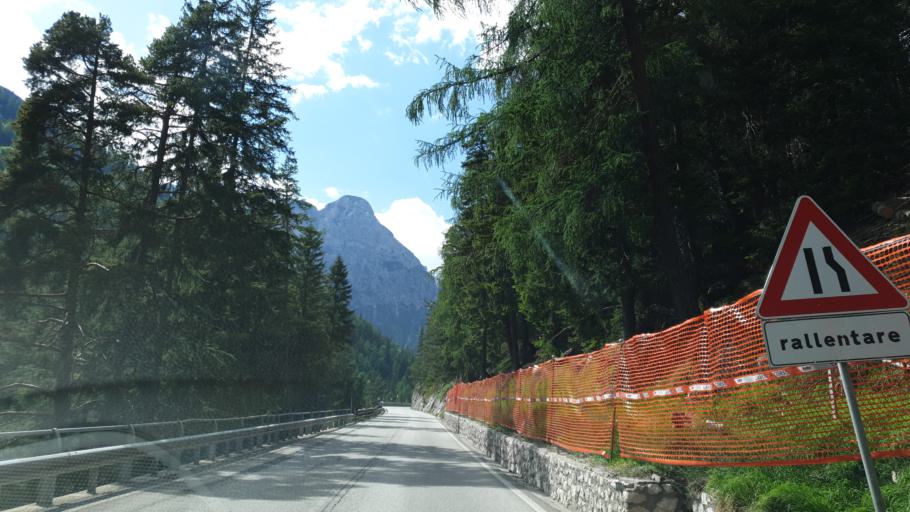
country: IT
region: Veneto
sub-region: Provincia di Belluno
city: Cortina d'Ampezzo
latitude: 46.5954
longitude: 12.1125
